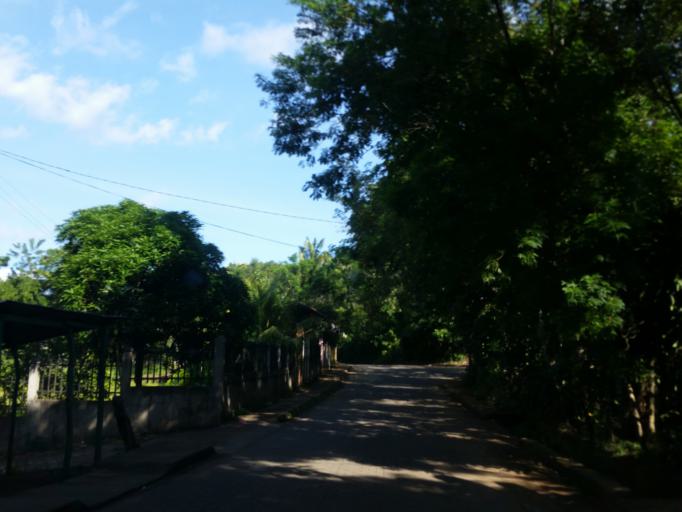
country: NI
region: Masaya
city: Catarina
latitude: 11.9362
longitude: -86.0713
